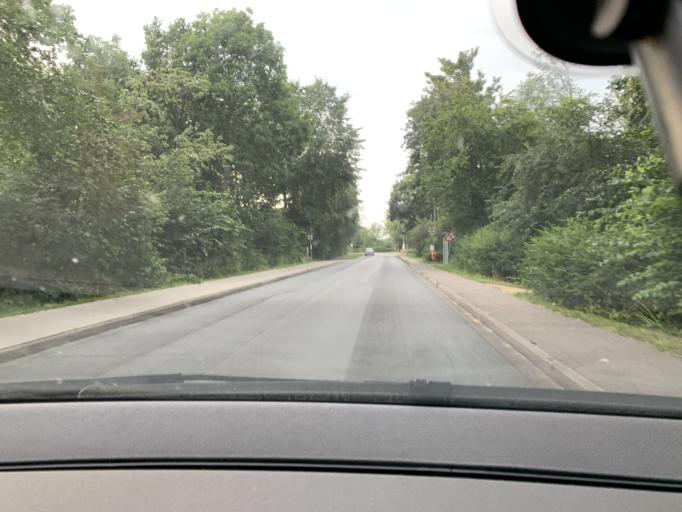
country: DE
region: Schleswig-Holstein
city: Mildstedt
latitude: 54.4654
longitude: 9.0931
